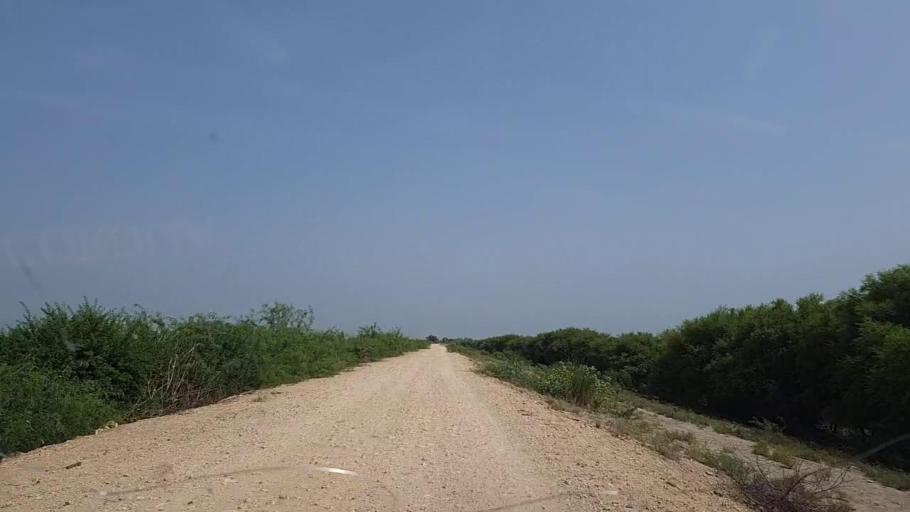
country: PK
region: Sindh
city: Ghotki
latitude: 28.0954
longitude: 69.4053
